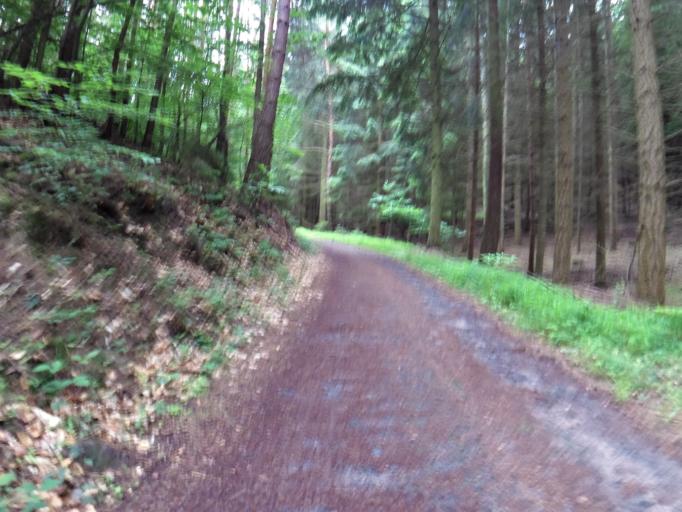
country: DE
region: Rheinland-Pfalz
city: Weisenheim am Berg
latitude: 49.5047
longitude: 8.1221
